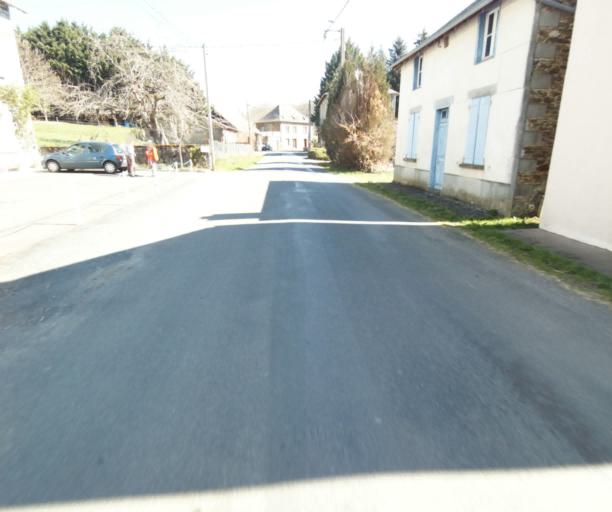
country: FR
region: Limousin
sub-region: Departement de la Correze
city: Saint-Clement
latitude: 45.3438
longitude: 1.6693
